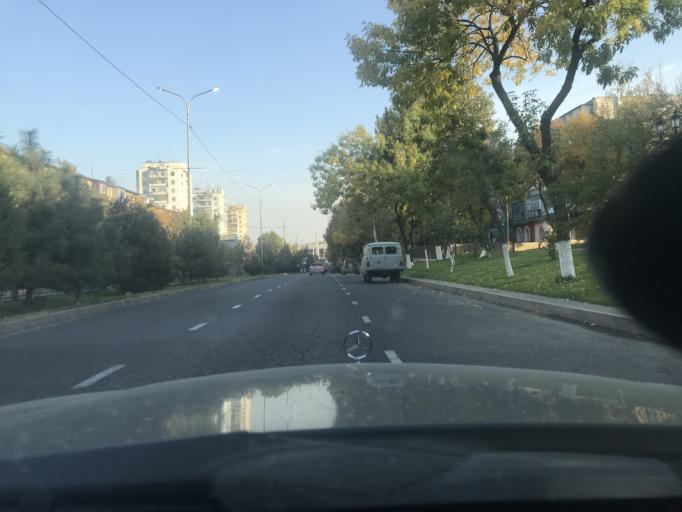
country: KZ
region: Ongtustik Qazaqstan
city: Shymkent
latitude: 42.3026
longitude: 69.6047
